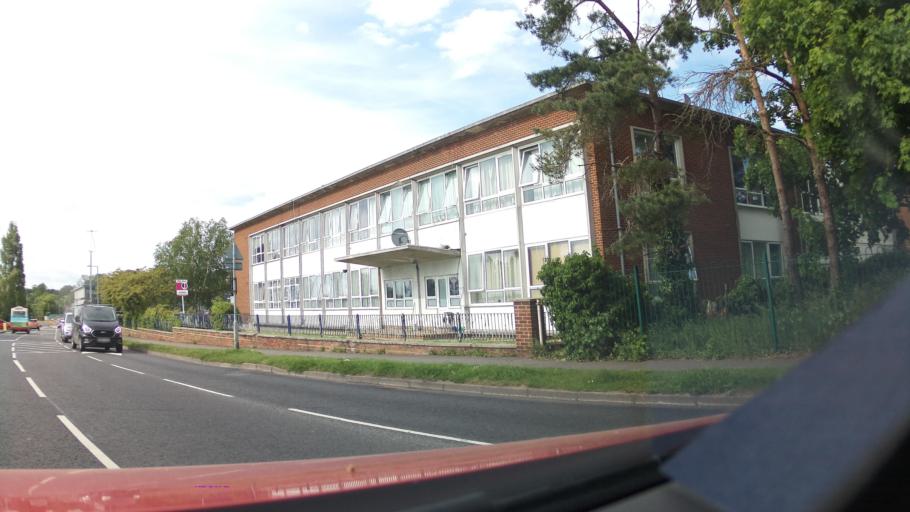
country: GB
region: England
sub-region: Worcestershire
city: Evesham
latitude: 52.1003
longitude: -1.9495
